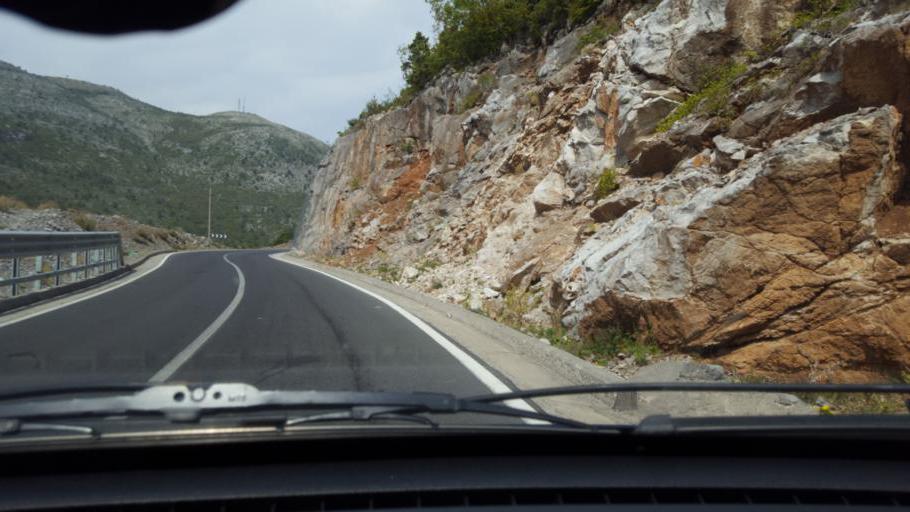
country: AL
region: Shkoder
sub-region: Rrethi i Malesia e Madhe
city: Kastrat
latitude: 42.3758
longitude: 19.4863
